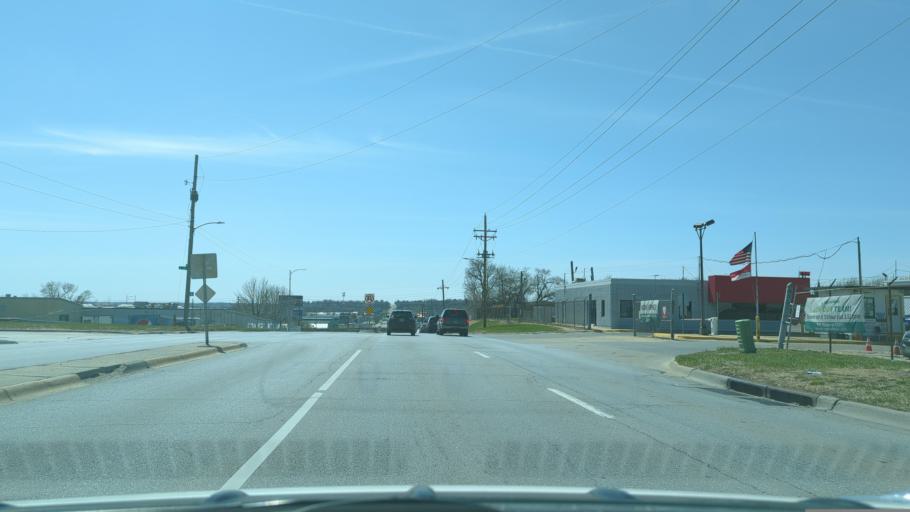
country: US
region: Nebraska
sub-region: Douglas County
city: Ralston
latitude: 41.2155
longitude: -96.0239
